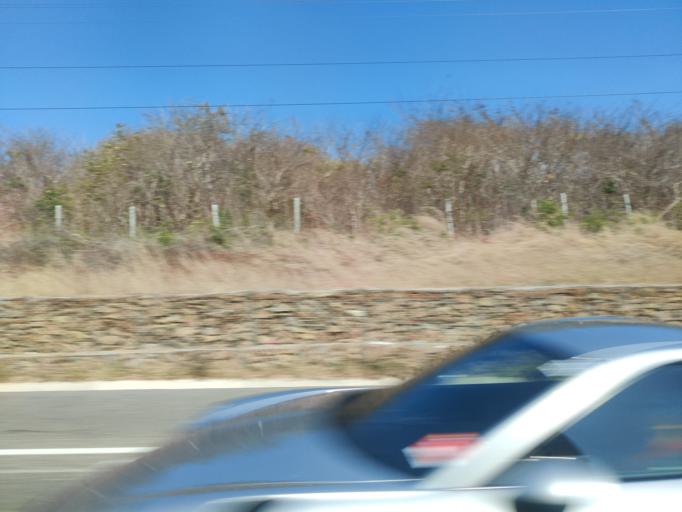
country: CO
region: Atlantico
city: Puerto Colombia
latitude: 10.9675
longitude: -74.9951
